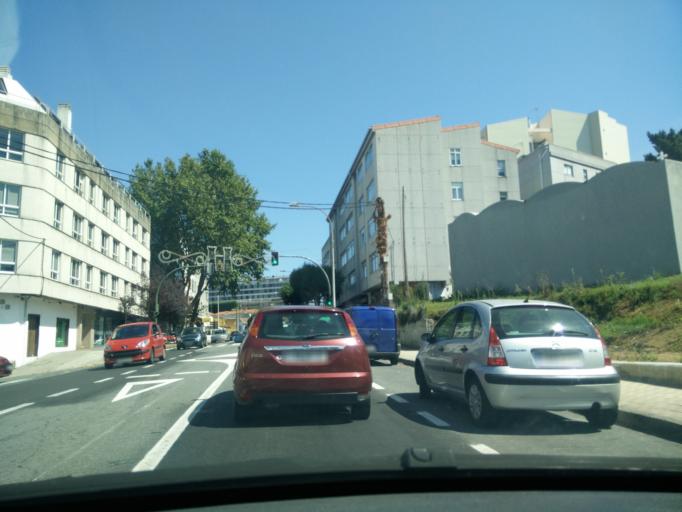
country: ES
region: Galicia
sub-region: Provincia da Coruna
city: A Coruna
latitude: 43.3366
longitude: -8.3746
